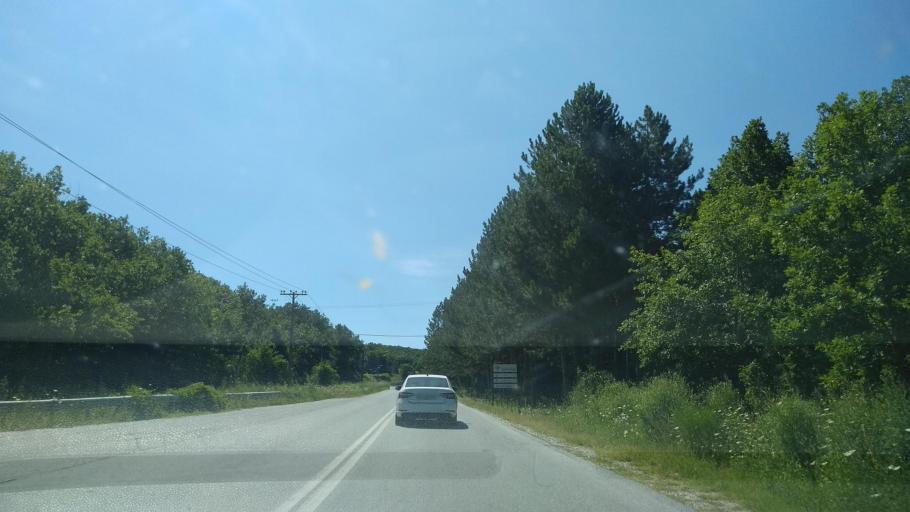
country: GR
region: Central Macedonia
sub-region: Nomos Chalkidikis
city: Megali Panagia
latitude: 40.4604
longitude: 23.6546
